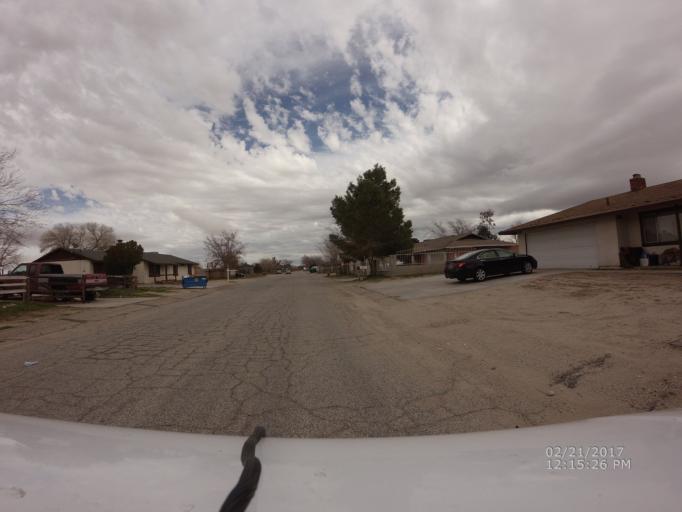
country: US
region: California
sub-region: Los Angeles County
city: Lake Los Angeles
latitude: 34.6324
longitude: -117.8589
